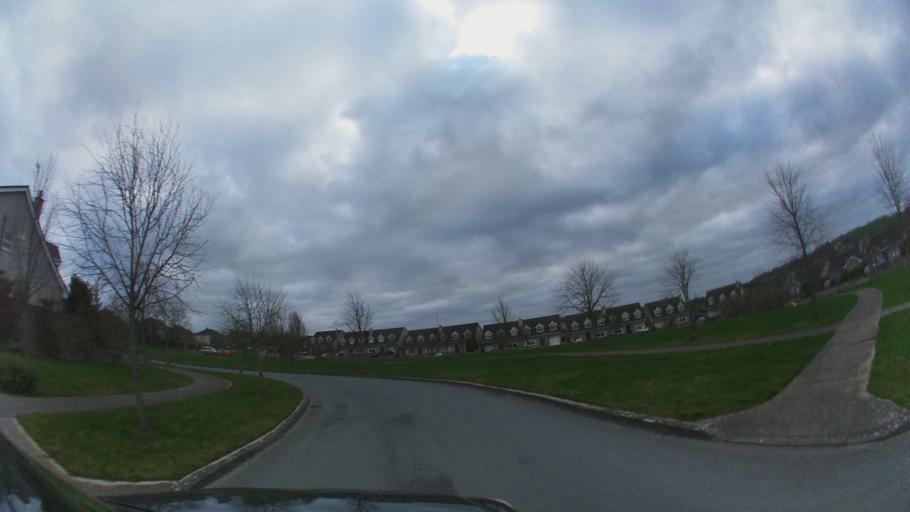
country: IE
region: Leinster
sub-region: An Mhi
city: Duleek
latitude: 53.6933
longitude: -6.4145
